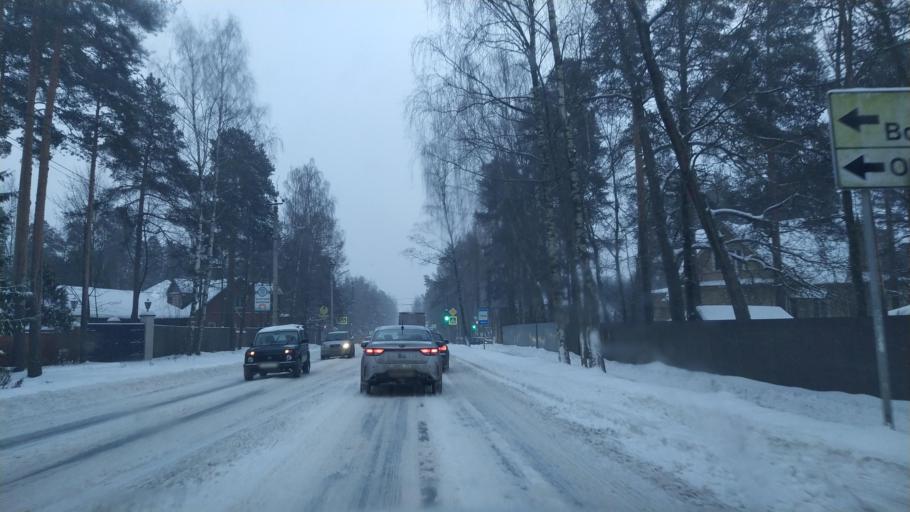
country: RU
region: Leningrad
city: Vsevolozhsk
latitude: 60.0207
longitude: 30.6564
